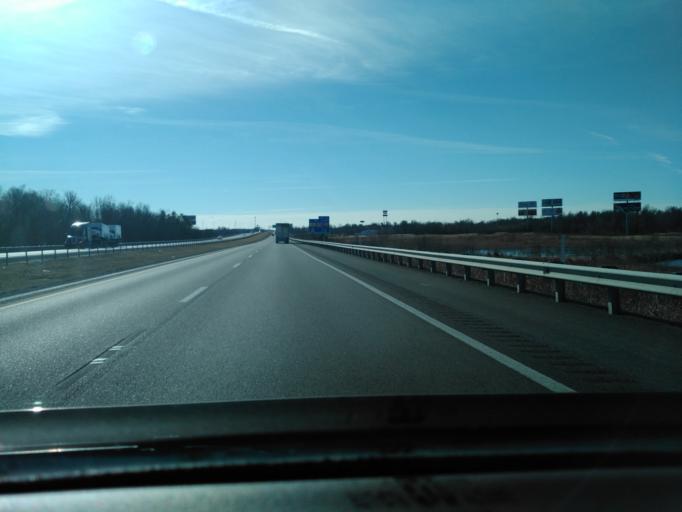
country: US
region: Illinois
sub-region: Massac County
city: Metropolis
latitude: 37.1060
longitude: -88.6914
